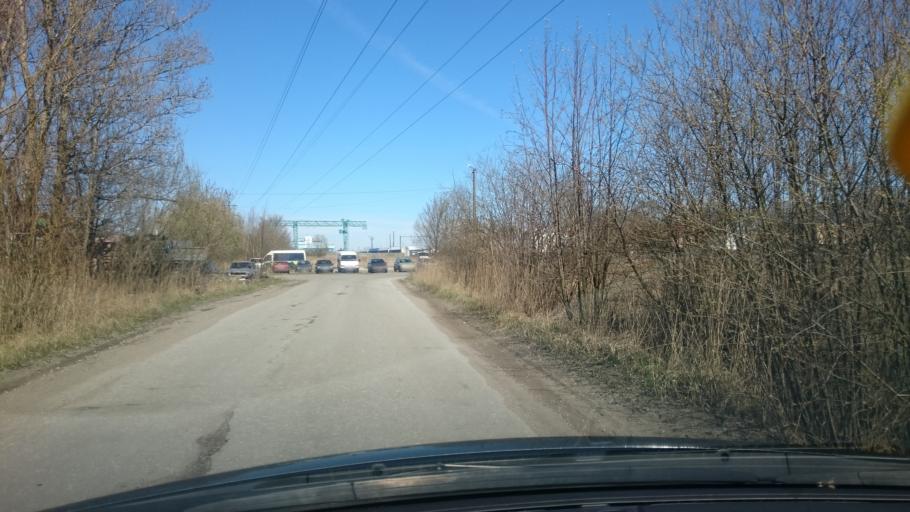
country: EE
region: Harju
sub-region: Tallinna linn
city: Tallinn
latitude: 59.4592
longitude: 24.6958
